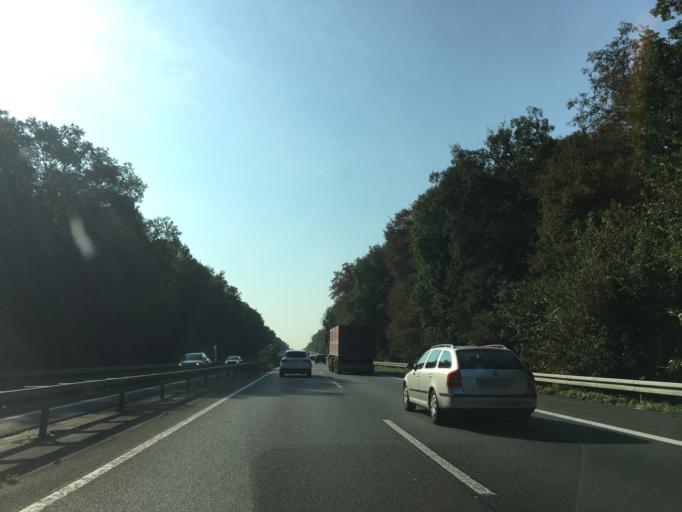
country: DE
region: Hesse
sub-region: Regierungsbezirk Darmstadt
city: Einhausen
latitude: 49.7079
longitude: 8.5468
